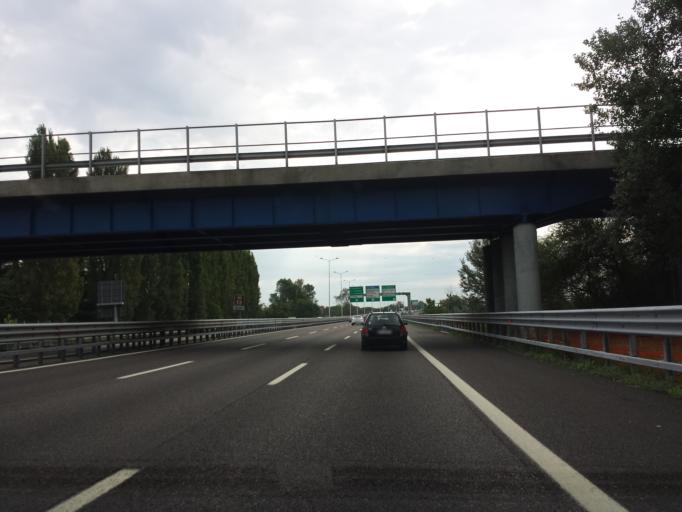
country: IT
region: Lombardy
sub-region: Citta metropolitana di Milano
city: Assago
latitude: 45.3980
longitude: 9.1322
